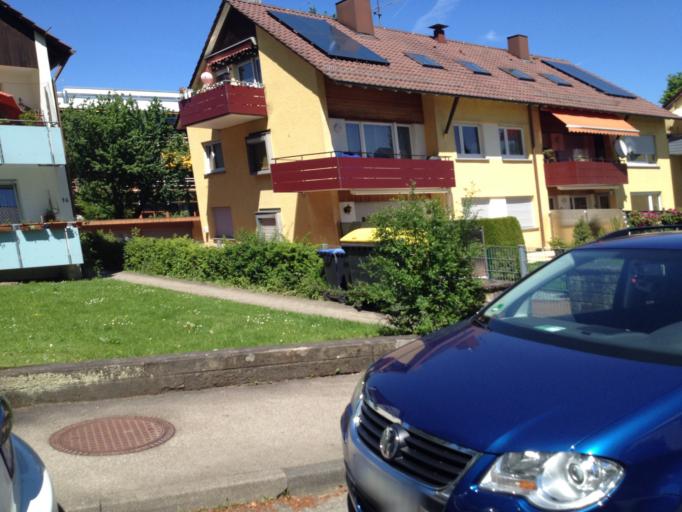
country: DE
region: Baden-Wuerttemberg
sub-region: Regierungsbezirk Stuttgart
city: Leinfelden-Echterdingen
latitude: 48.6981
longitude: 9.1360
